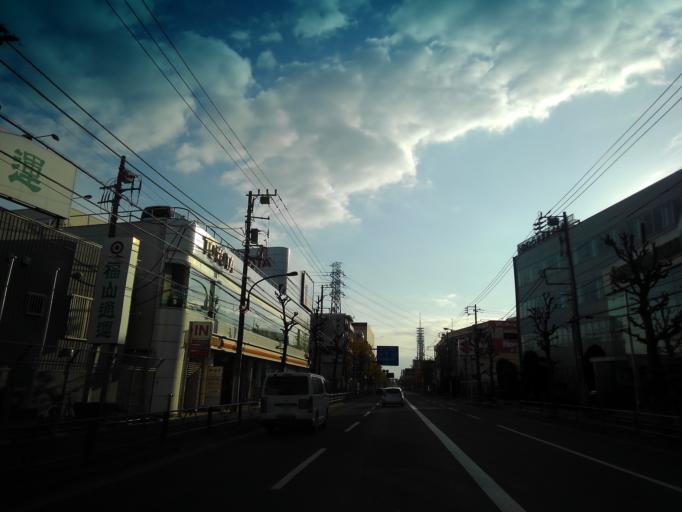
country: JP
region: Tokyo
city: Tanashicho
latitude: 35.7394
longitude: 139.5084
